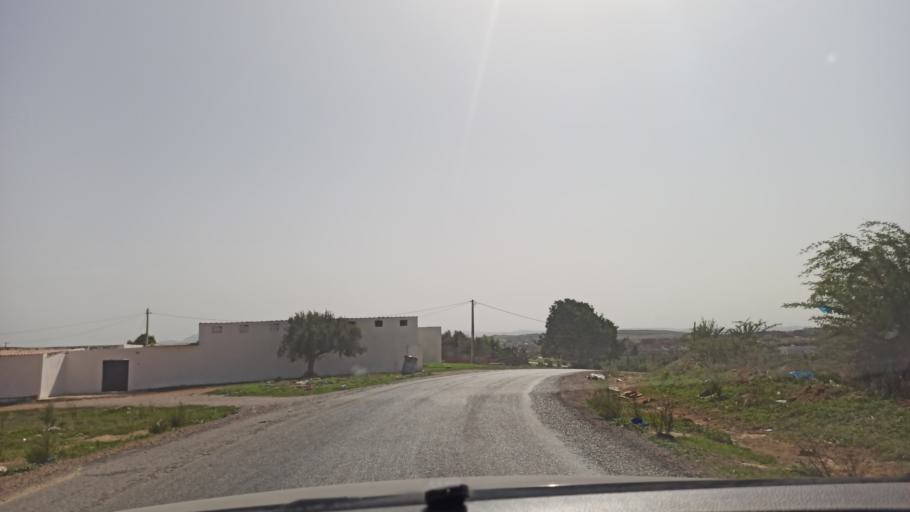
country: TN
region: Manouba
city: Manouba
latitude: 36.7337
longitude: 10.0937
